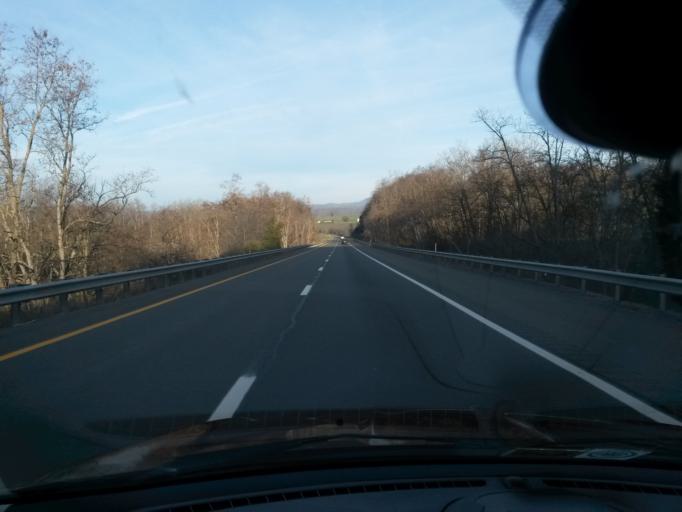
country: US
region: West Virginia
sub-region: Greenbrier County
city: Lewisburg
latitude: 37.8339
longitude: -80.4577
